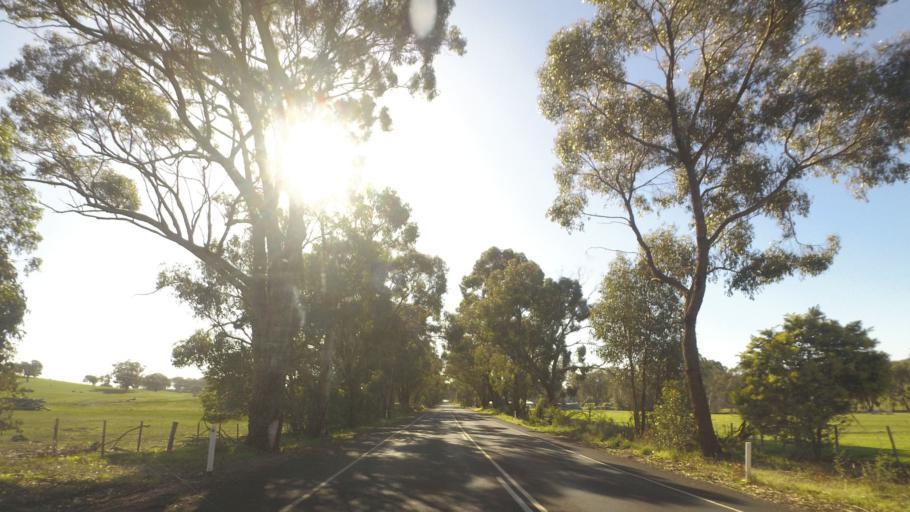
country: AU
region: Victoria
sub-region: Greater Bendigo
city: Kennington
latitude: -36.8916
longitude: 144.3126
